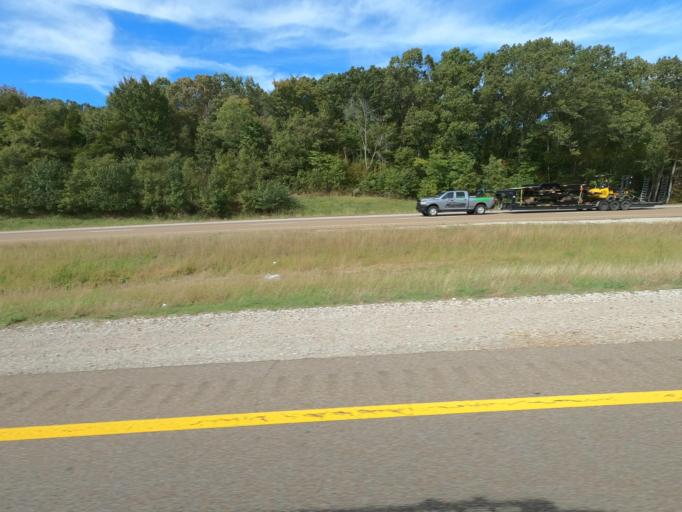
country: US
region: Tennessee
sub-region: Shelby County
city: Arlington
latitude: 35.2691
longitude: -89.6514
